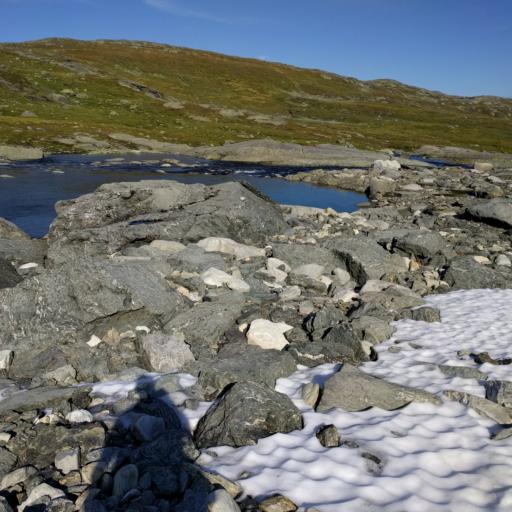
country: NO
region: Aust-Agder
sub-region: Bykle
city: Hovden
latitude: 59.9213
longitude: 7.2075
